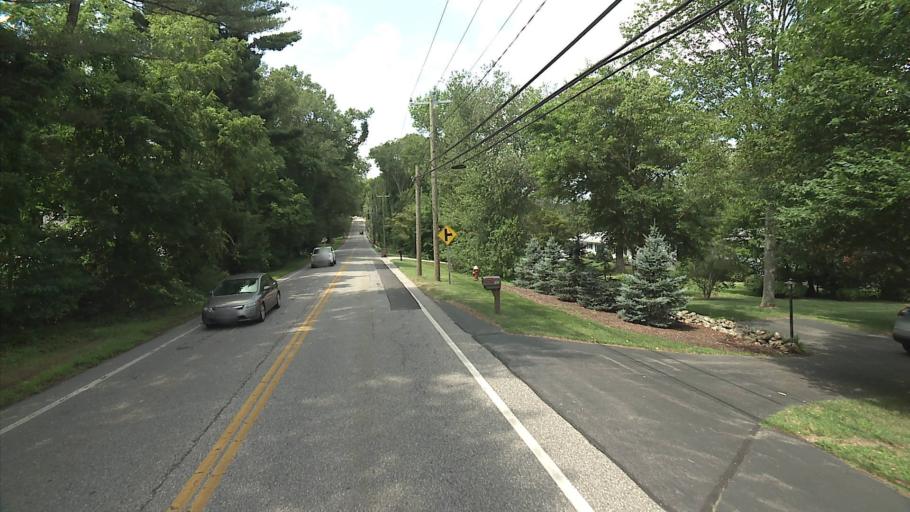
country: US
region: Connecticut
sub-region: New London County
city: Niantic
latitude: 41.3775
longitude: -72.2138
